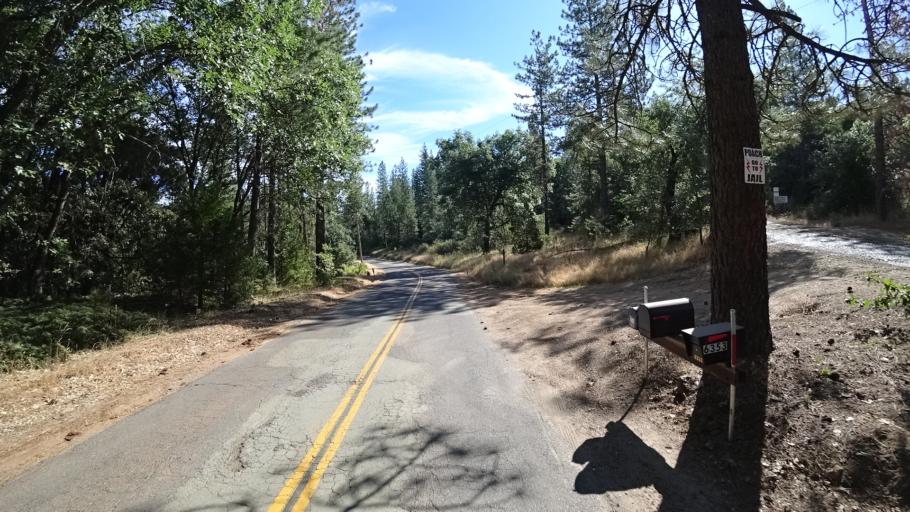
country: US
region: California
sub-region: Amador County
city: Pioneer
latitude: 38.3760
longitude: -120.4527
